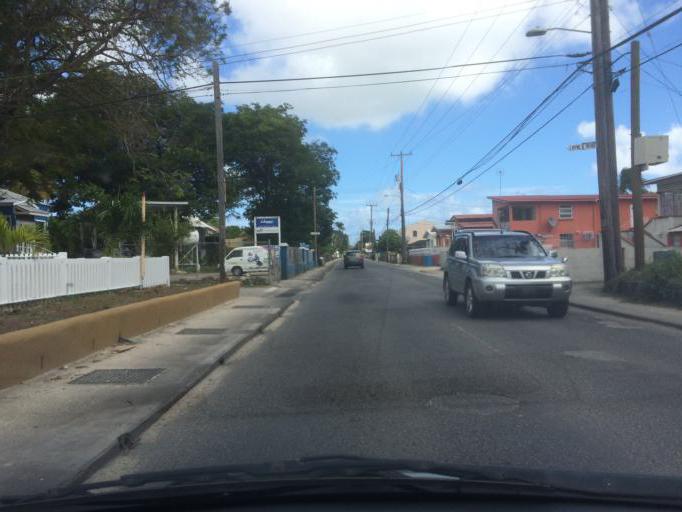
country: BB
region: Christ Church
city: Oistins
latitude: 13.0695
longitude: -59.5623
